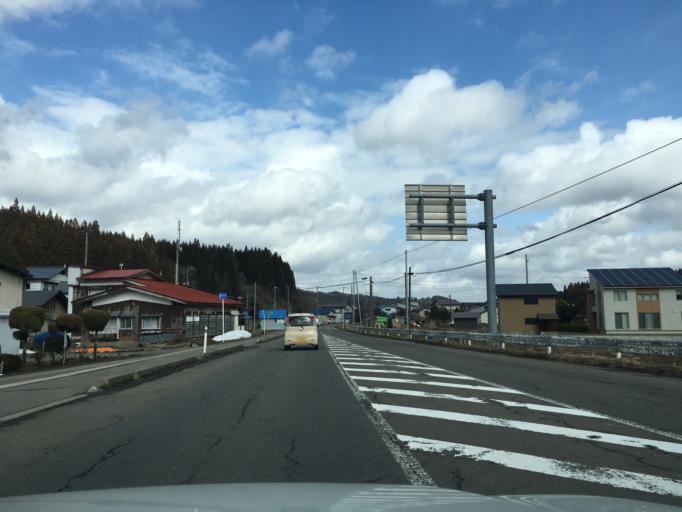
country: JP
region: Akita
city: Takanosu
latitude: 40.0326
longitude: 140.2748
